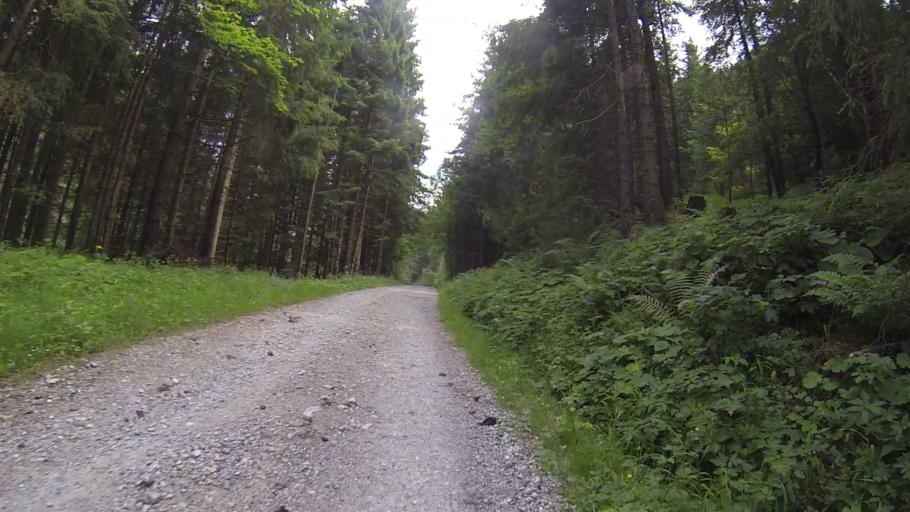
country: AT
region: Tyrol
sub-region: Politischer Bezirk Reutte
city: Jungholz
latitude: 47.5977
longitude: 10.4712
